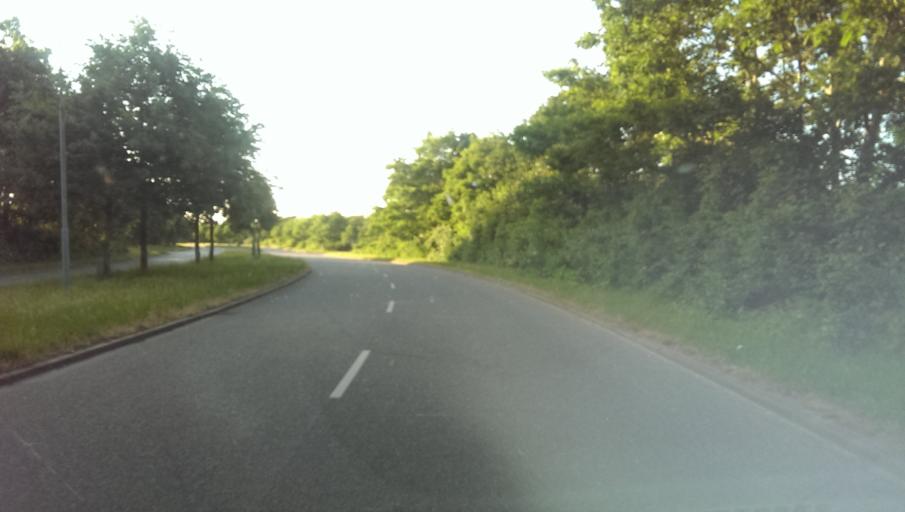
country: DK
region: South Denmark
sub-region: Esbjerg Kommune
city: Esbjerg
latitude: 55.5138
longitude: 8.4503
